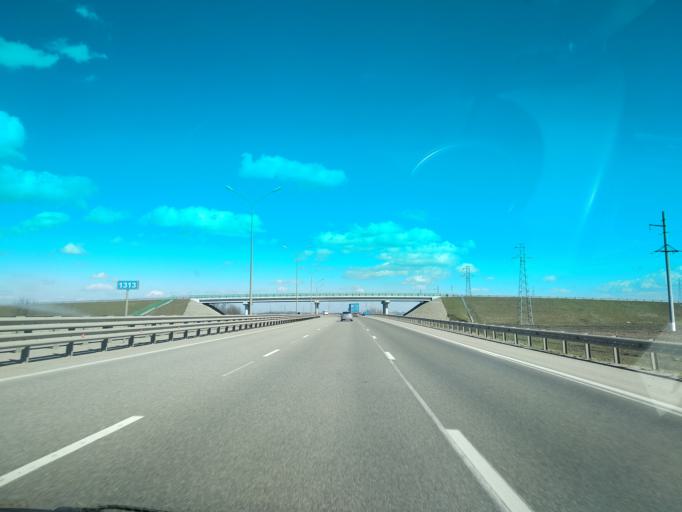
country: RU
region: Krasnodarskiy
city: Dinskaya
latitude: 45.2169
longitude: 39.1726
